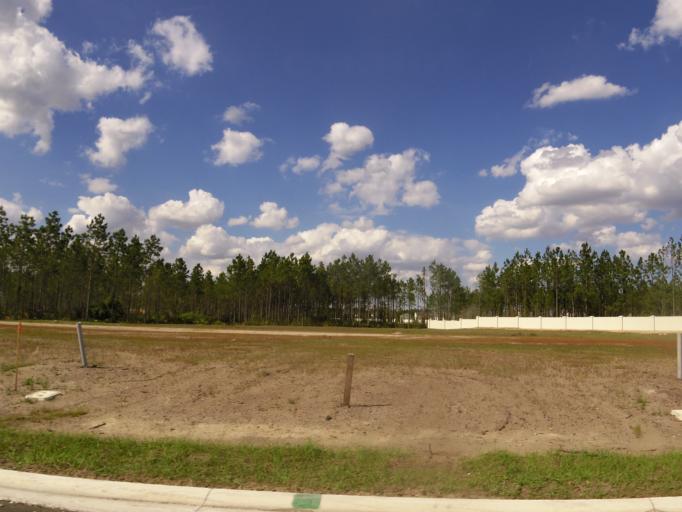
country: US
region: Florida
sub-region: Saint Johns County
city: Palm Valley
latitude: 30.1933
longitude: -81.5070
